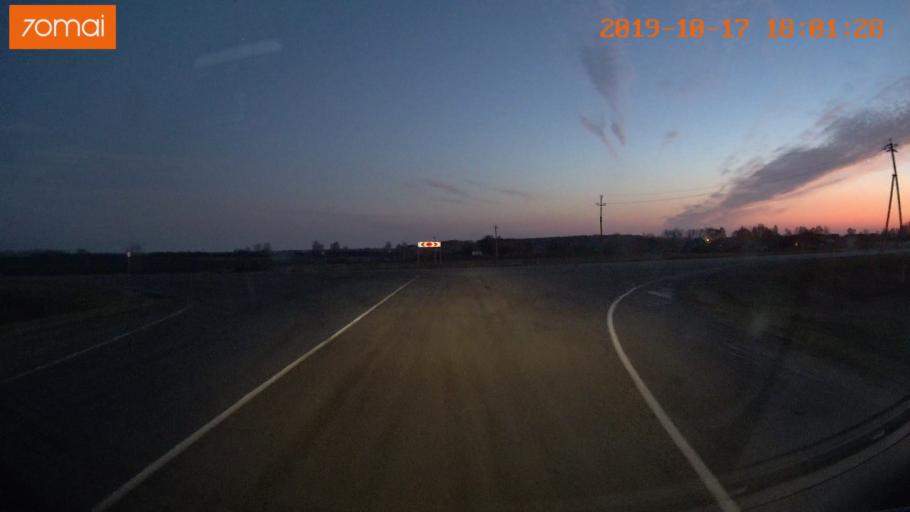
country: RU
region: Tula
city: Kurkino
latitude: 53.5078
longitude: 38.6099
